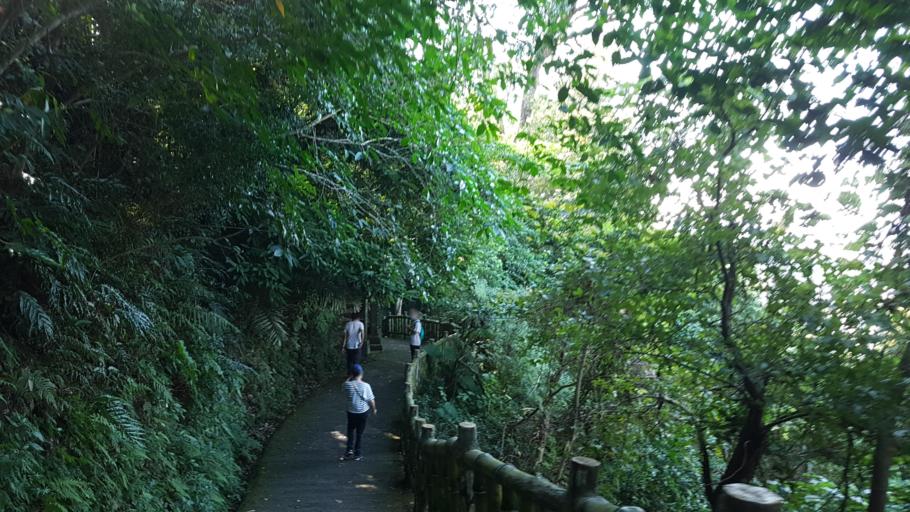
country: TW
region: Taipei
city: Taipei
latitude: 24.9921
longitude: 121.5472
